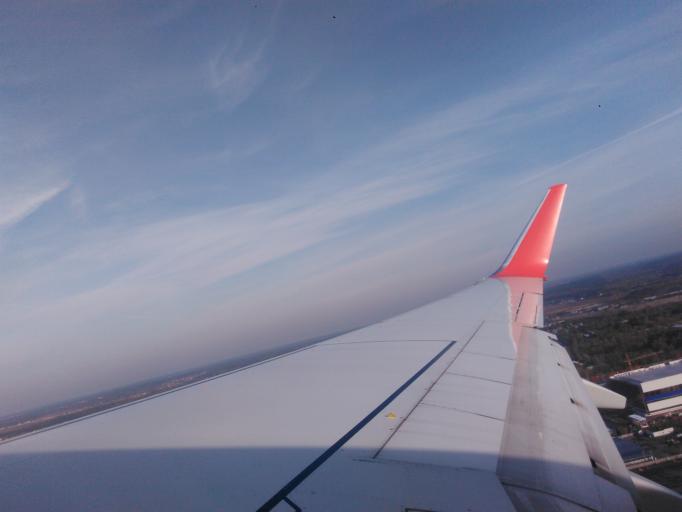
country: RU
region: Moskovskaya
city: Novopodrezkovo
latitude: 55.9700
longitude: 37.3918
